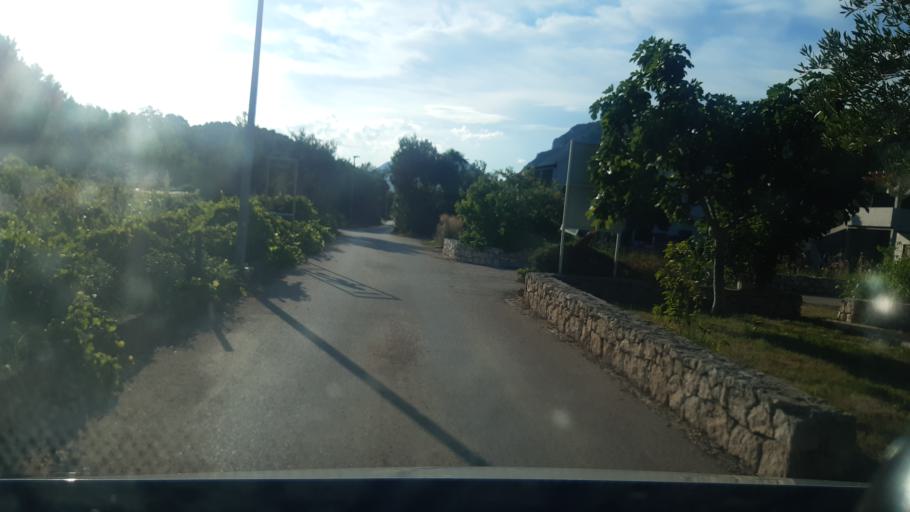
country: HR
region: Dubrovacko-Neretvanska
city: Blato
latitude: 42.8883
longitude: 17.4577
